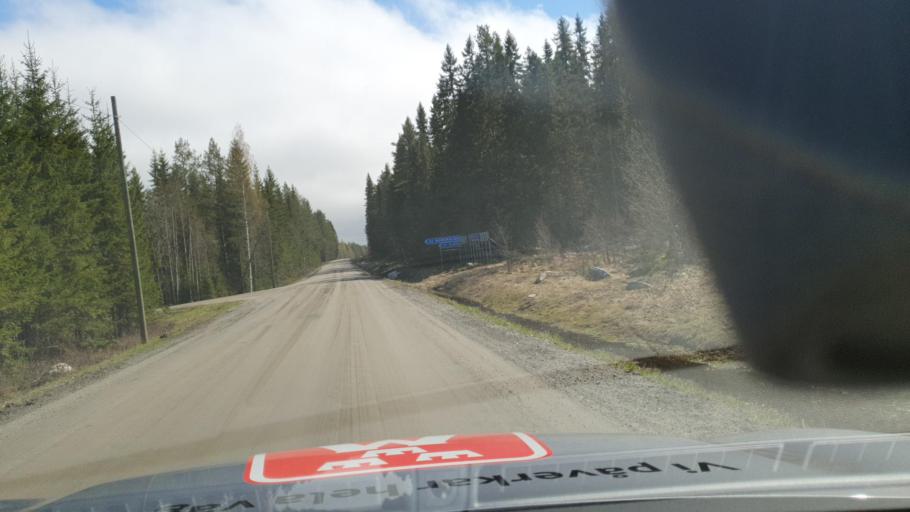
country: SE
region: Vaesterbotten
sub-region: Bjurholms Kommun
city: Bjurholm
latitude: 63.6796
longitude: 18.9868
